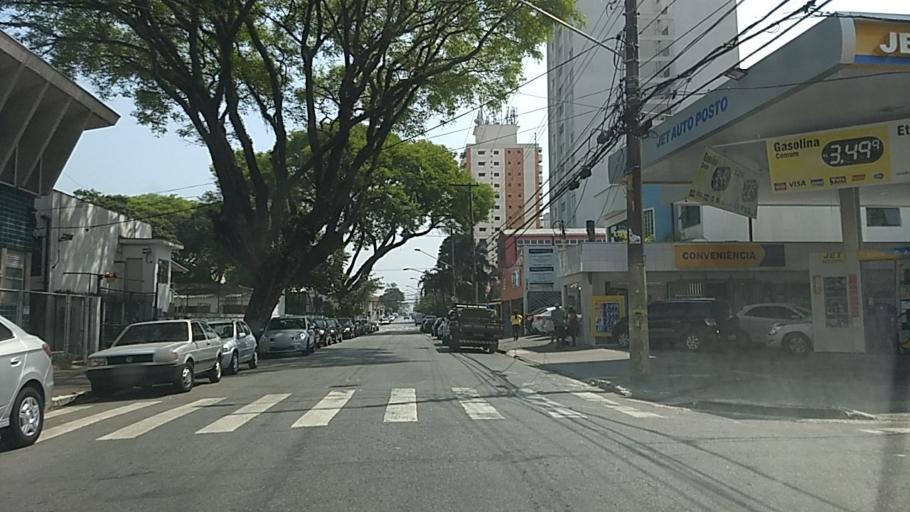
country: BR
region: Sao Paulo
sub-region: Sao Paulo
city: Sao Paulo
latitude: -23.5328
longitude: -46.5659
